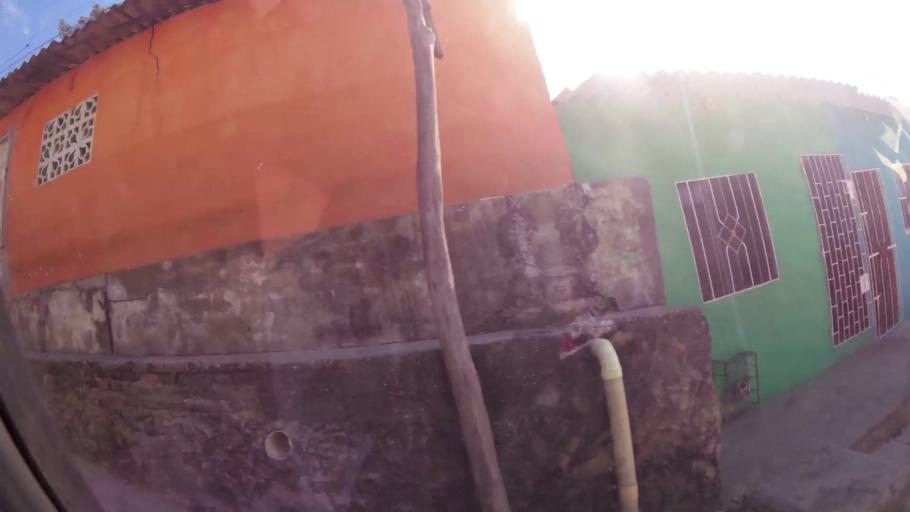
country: CO
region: Atlantico
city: Soledad
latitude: 10.9265
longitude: -74.8167
